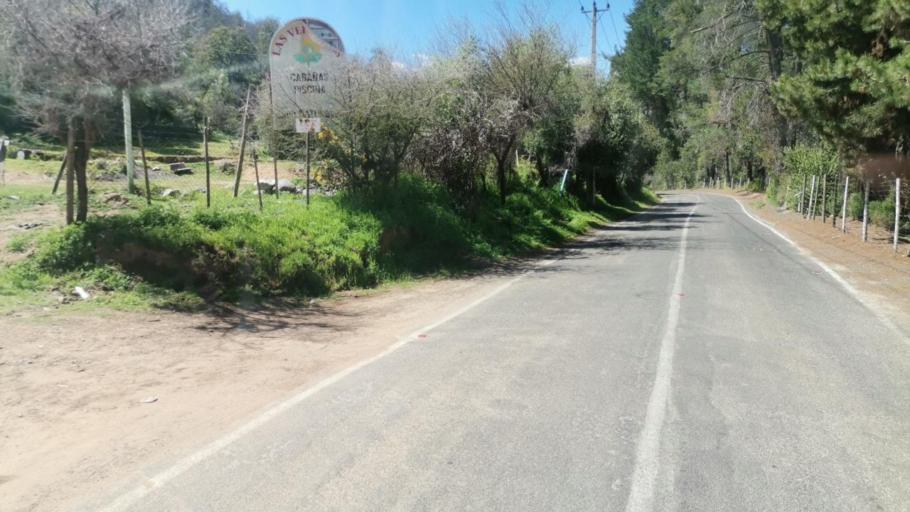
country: CL
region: Valparaiso
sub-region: Provincia de Marga Marga
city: Limache
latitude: -33.1788
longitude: -71.1731
